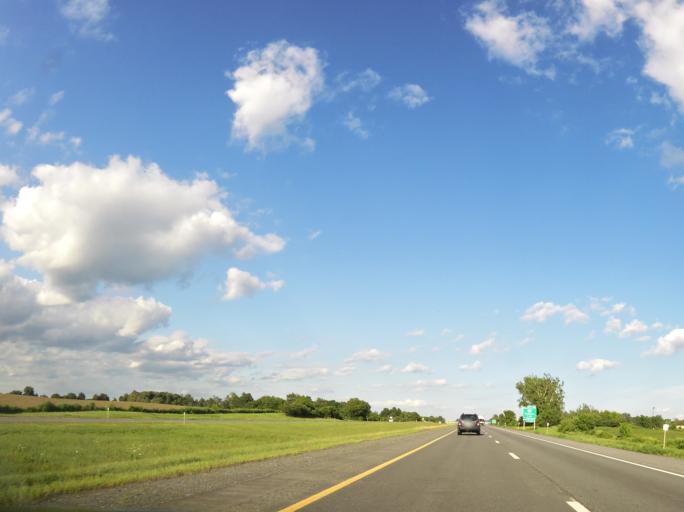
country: US
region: New York
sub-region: Genesee County
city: Batavia
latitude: 43.0177
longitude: -78.2097
